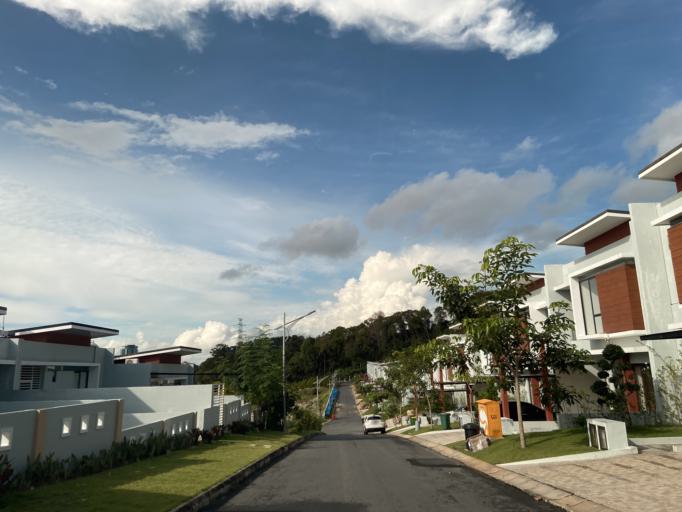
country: SG
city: Singapore
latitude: 1.0941
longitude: 104.0272
